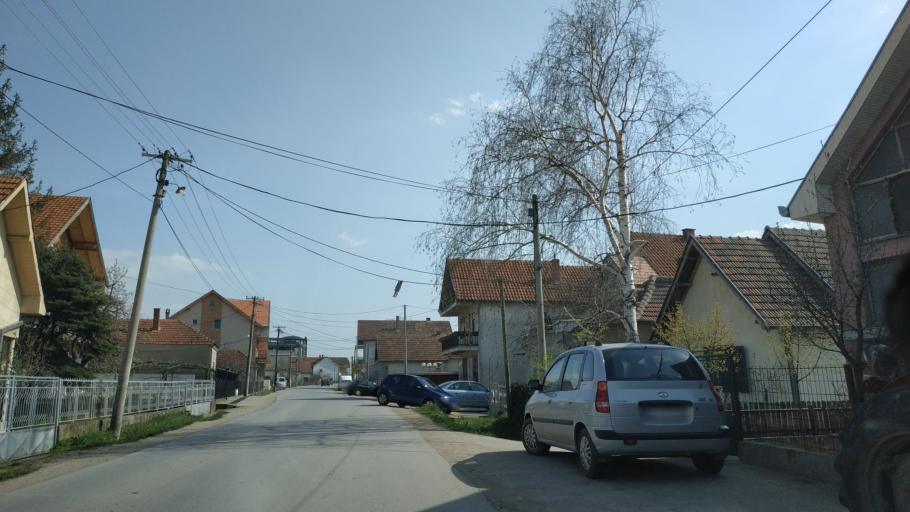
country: RS
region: Central Serbia
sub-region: Nisavski Okrug
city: Aleksinac
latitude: 43.5109
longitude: 21.6915
